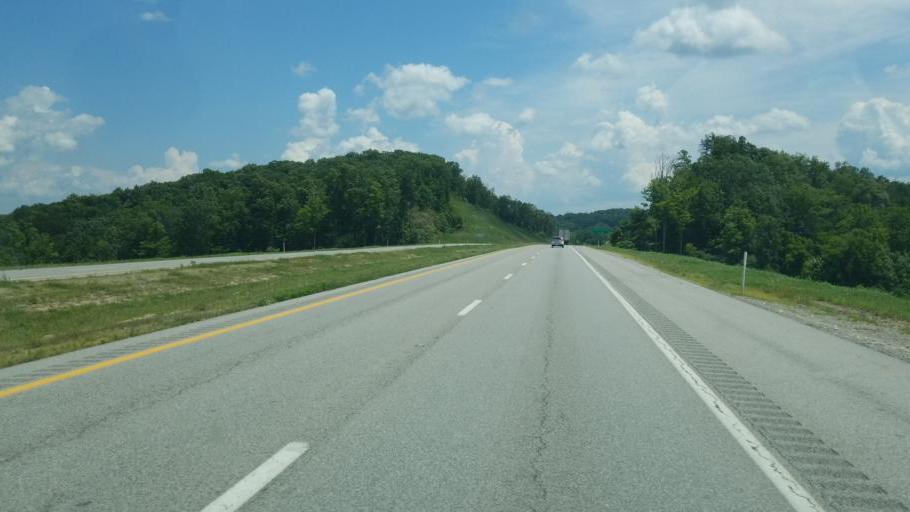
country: US
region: West Virginia
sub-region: Mason County
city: Point Pleasant
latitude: 38.7847
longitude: -82.0791
